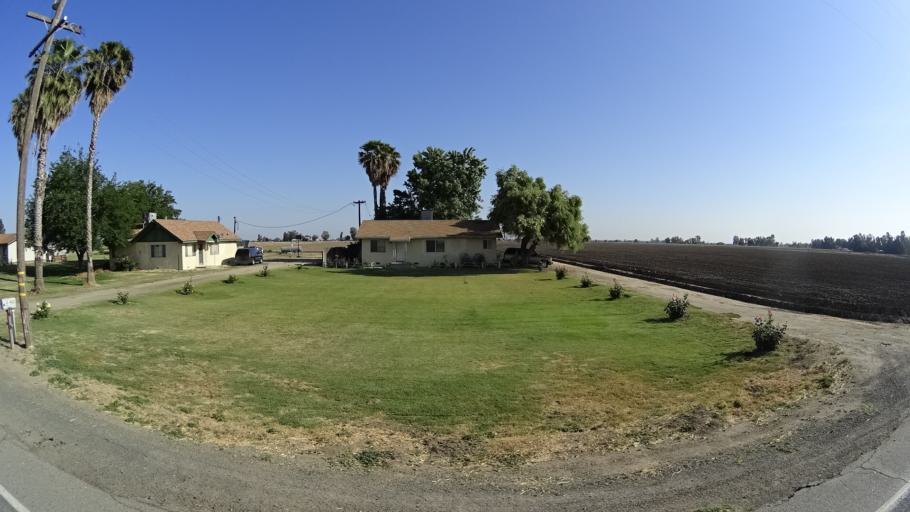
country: US
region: California
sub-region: Kings County
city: Lemoore Station
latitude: 36.3439
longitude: -119.8766
